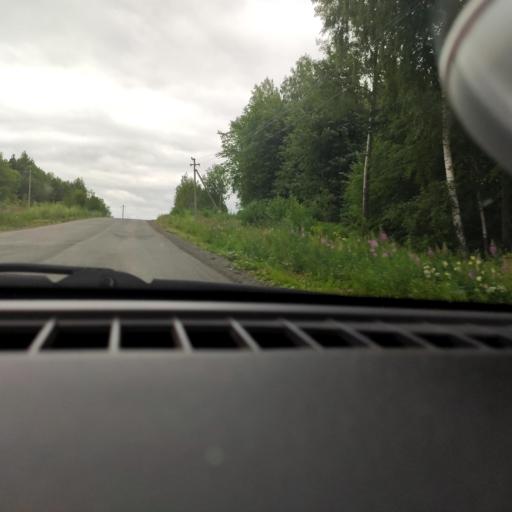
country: RU
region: Perm
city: Polazna
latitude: 58.3333
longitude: 56.1571
